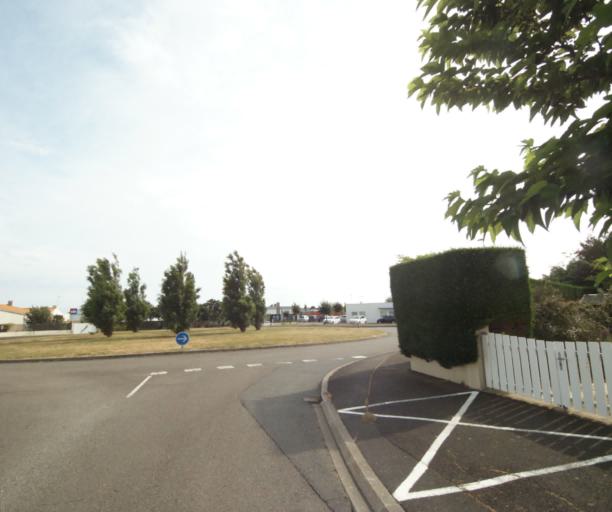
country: FR
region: Pays de la Loire
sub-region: Departement de la Vendee
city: Chateau-d'Olonne
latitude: 46.4887
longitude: -1.7446
